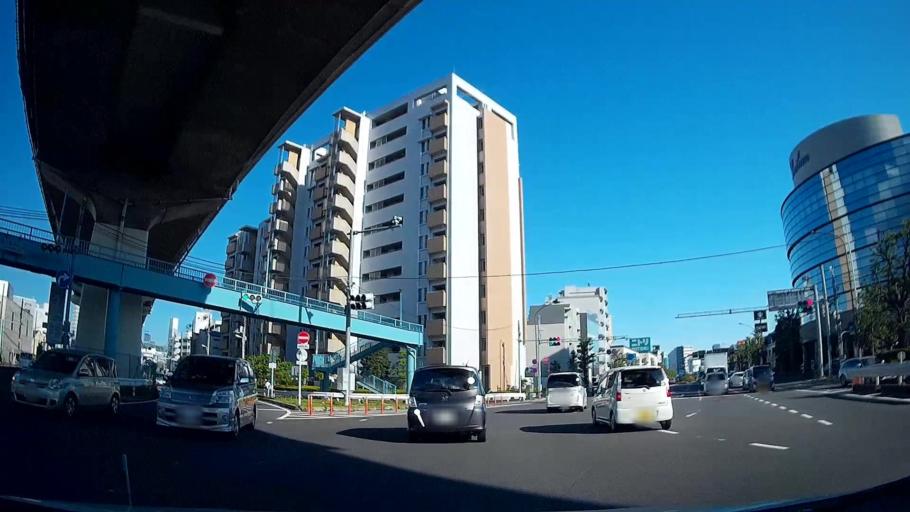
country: JP
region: Tokyo
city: Chofugaoka
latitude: 35.6274
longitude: 139.6264
